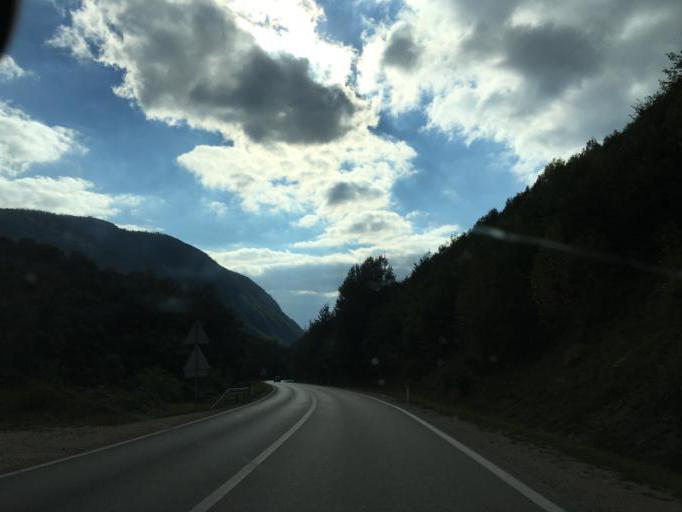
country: BA
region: Federation of Bosnia and Herzegovina
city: Bugojno
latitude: 44.0937
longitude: 17.5611
